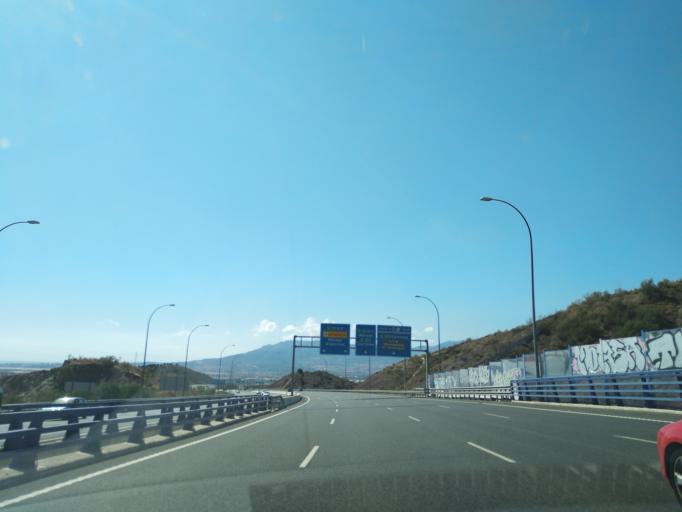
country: ES
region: Andalusia
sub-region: Provincia de Malaga
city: Malaga
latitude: 36.7352
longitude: -4.5066
